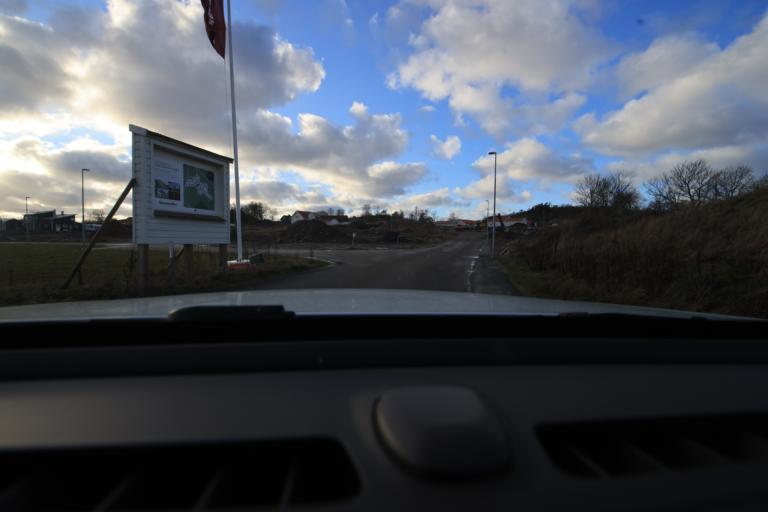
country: SE
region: Halland
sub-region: Varbergs Kommun
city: Varberg
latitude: 57.1371
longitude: 12.2999
